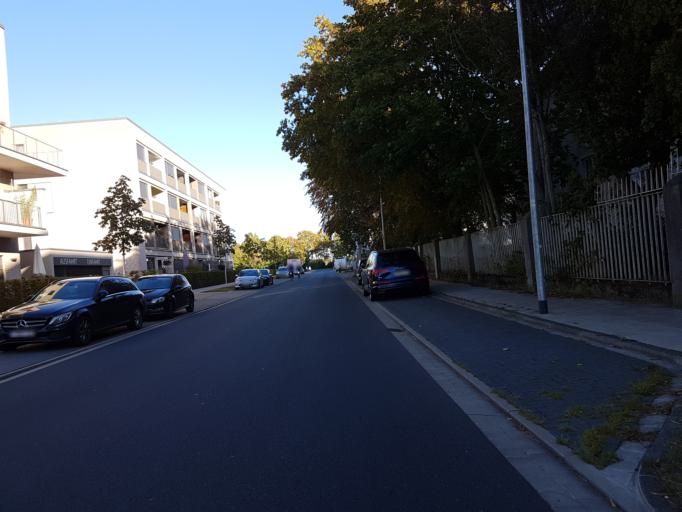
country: DE
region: Lower Saxony
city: Hannover
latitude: 52.4039
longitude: 9.7455
